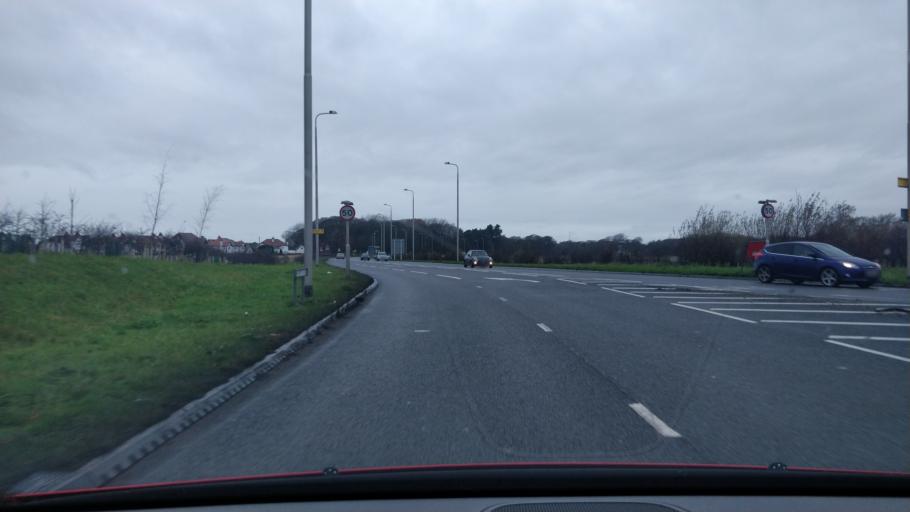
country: GB
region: England
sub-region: Sefton
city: Thornton
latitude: 53.5052
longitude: -3.0025
